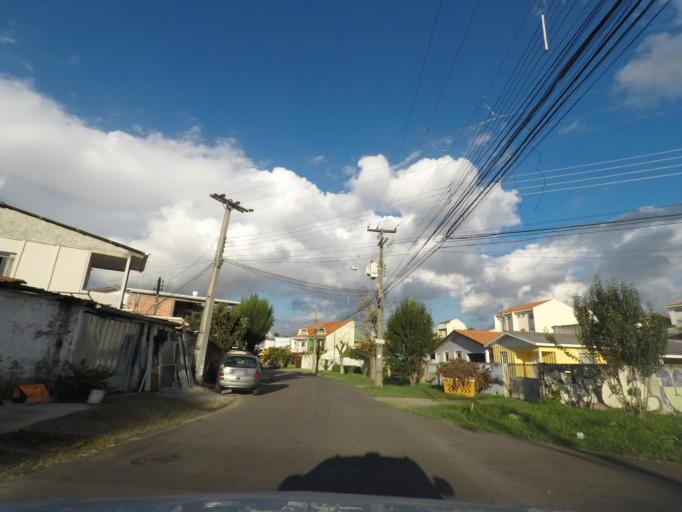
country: BR
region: Parana
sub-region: Sao Jose Dos Pinhais
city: Sao Jose dos Pinhais
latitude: -25.4989
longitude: -49.2615
